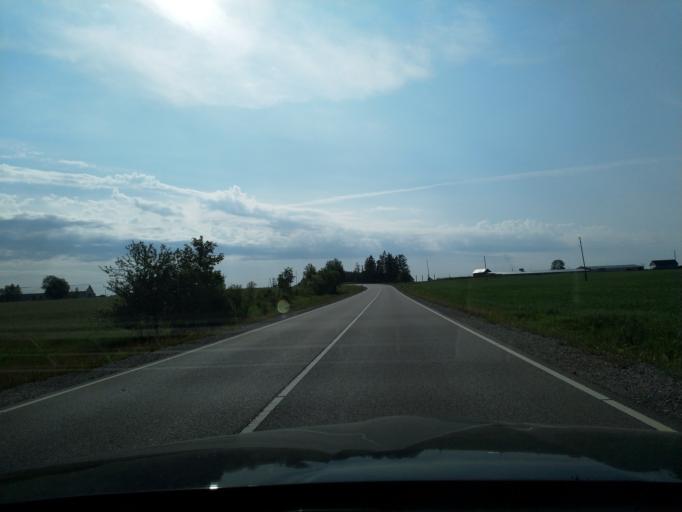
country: LV
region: Talsu Rajons
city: Sabile
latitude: 56.9440
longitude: 22.4138
